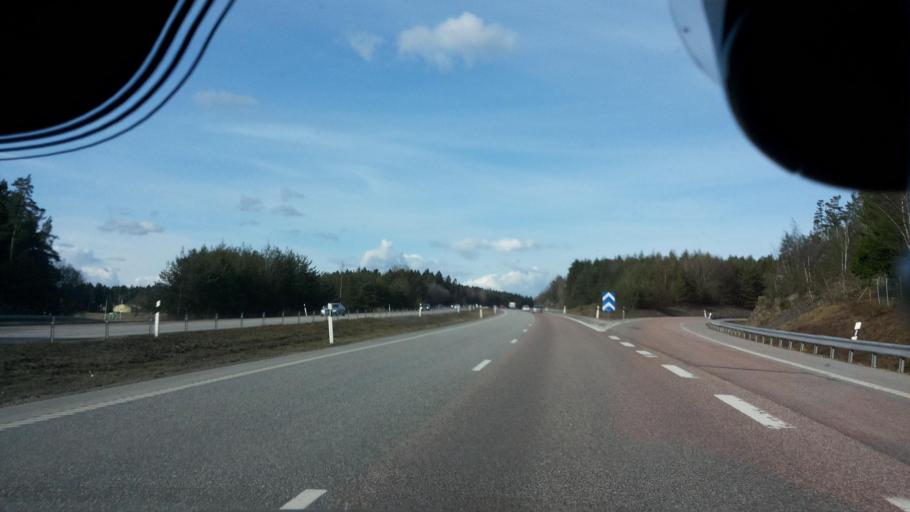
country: SE
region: Soedermanland
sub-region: Trosa Kommun
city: Vagnharad
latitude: 59.0222
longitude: 17.5541
